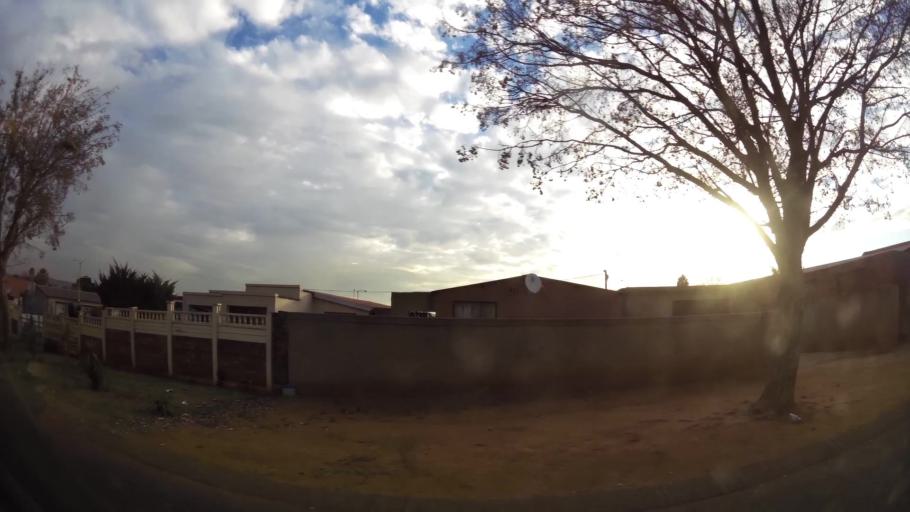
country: ZA
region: Gauteng
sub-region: City of Tshwane Metropolitan Municipality
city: Pretoria
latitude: -25.7033
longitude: 28.3179
